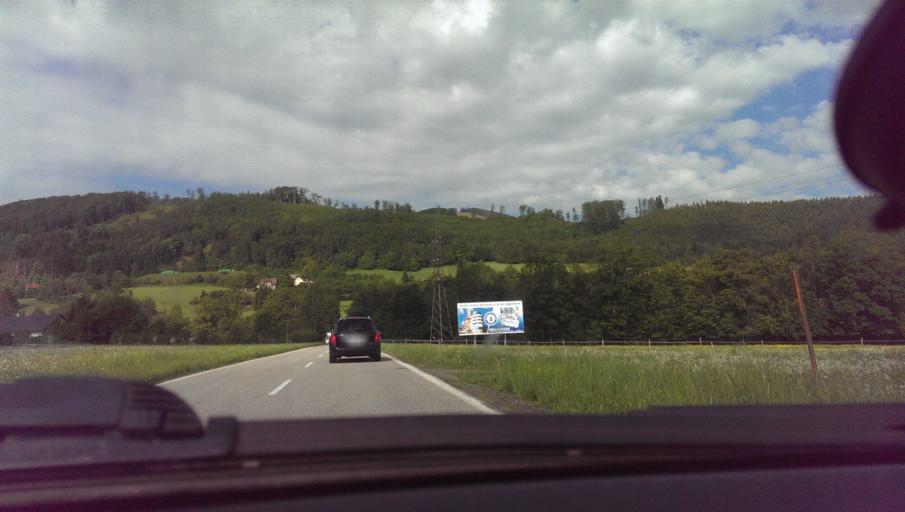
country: CZ
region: Moravskoslezsky
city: Frenstat pod Radhostem
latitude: 49.5156
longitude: 18.2017
